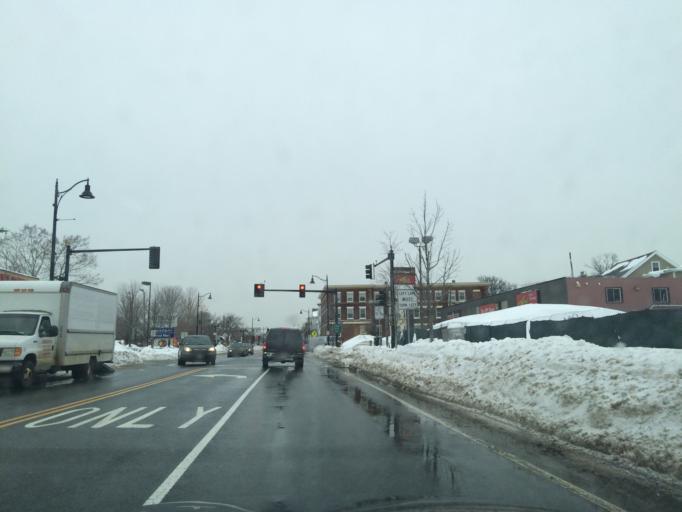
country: US
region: Massachusetts
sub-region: Middlesex County
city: Somerville
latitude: 42.3831
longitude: -71.1057
